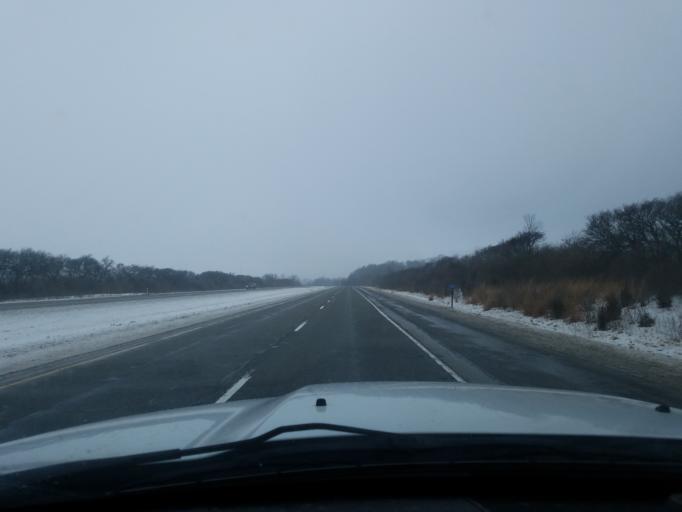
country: US
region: Indiana
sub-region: Fulton County
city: Rochester
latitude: 41.0364
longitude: -86.1916
